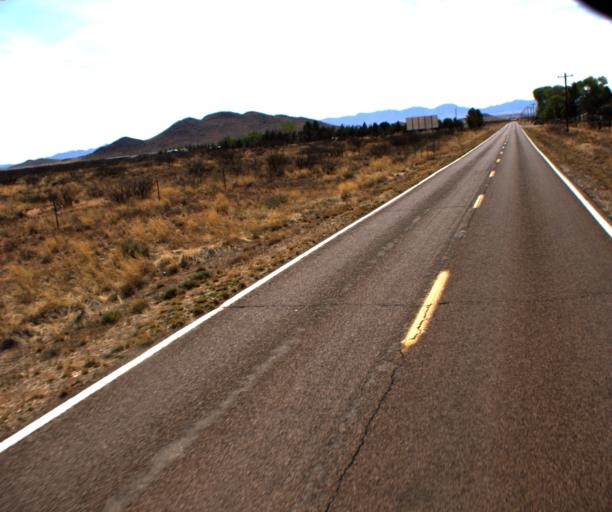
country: US
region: Arizona
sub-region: Cochise County
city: Willcox
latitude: 31.8763
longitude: -109.6335
